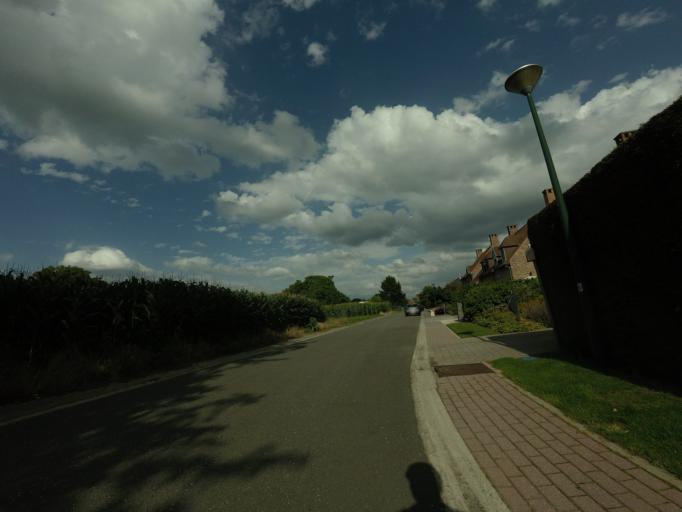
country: BE
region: Flanders
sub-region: Provincie Vlaams-Brabant
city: Grimbergen
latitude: 50.9455
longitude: 4.3670
